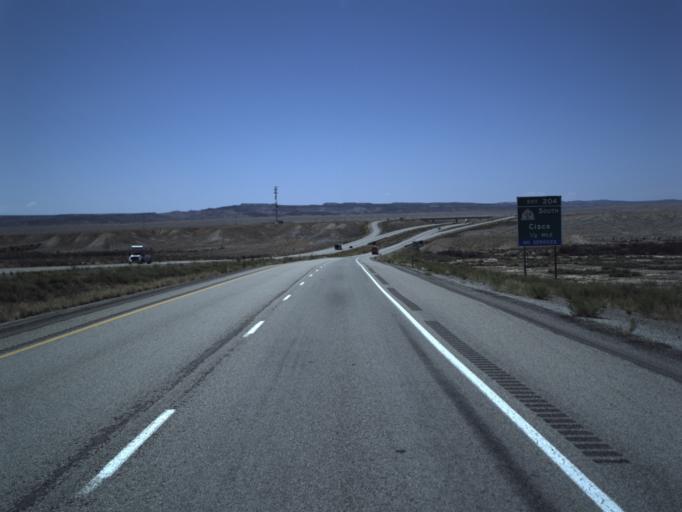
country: US
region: Utah
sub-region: Grand County
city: Moab
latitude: 38.9461
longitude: -109.3973
